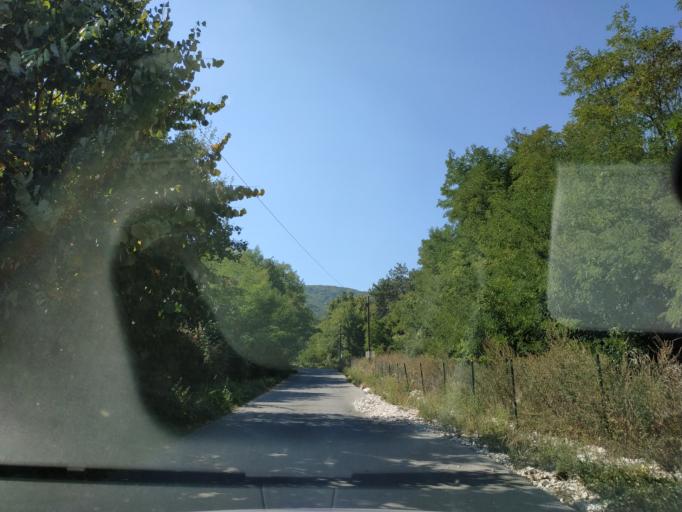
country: RS
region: Central Serbia
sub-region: Sumadijski Okrug
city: Arangelovac
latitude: 44.2995
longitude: 20.5475
